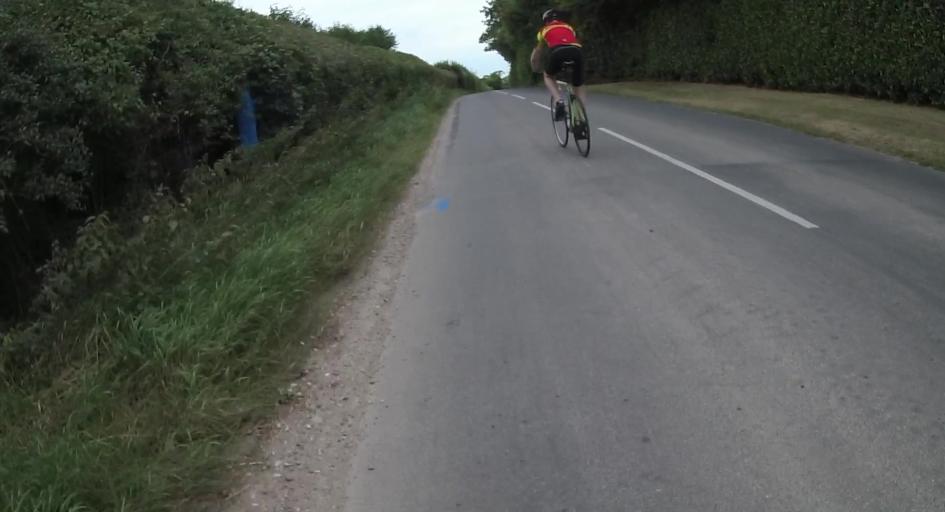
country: GB
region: England
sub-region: Hampshire
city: Kings Worthy
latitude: 51.1244
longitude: -1.3103
